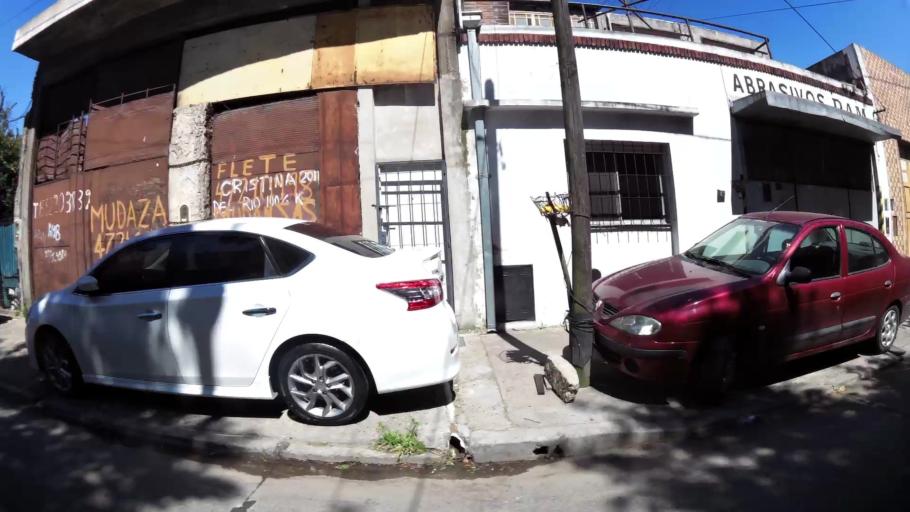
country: AR
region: Buenos Aires
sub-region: Partido de General San Martin
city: General San Martin
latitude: -34.5312
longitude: -58.5311
